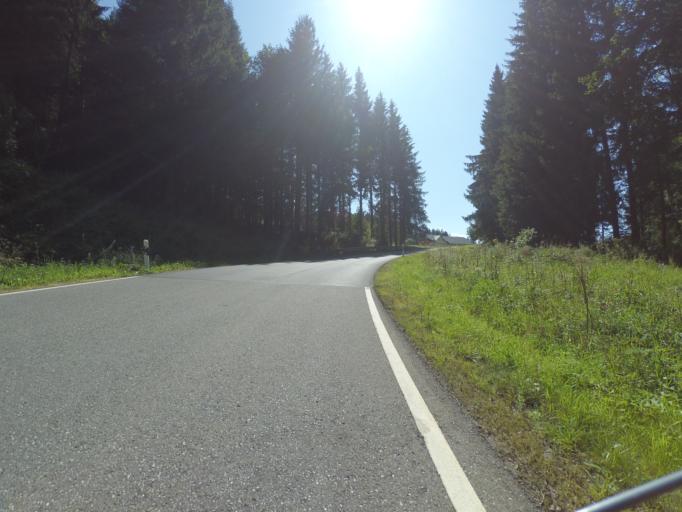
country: DE
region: Baden-Wuerttemberg
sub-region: Freiburg Region
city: Eisenbach
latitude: 47.9712
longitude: 8.2230
